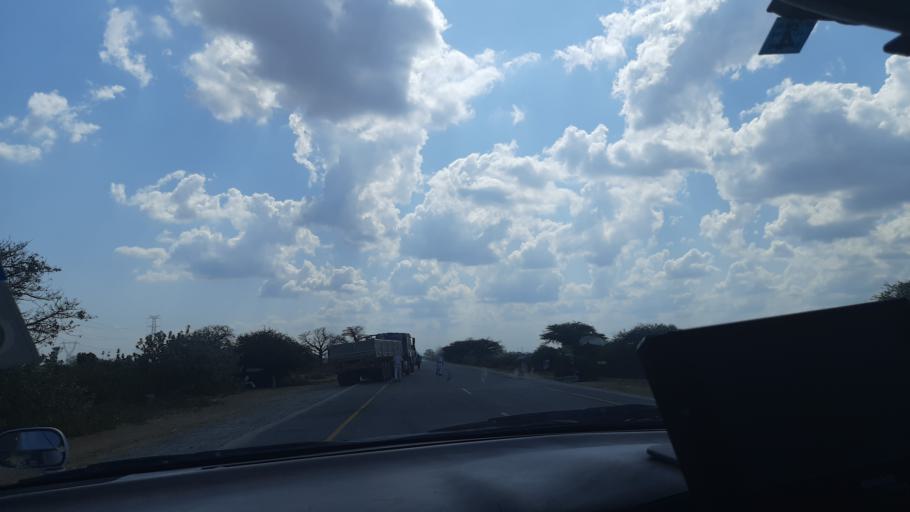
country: TZ
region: Singida
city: Kintinku
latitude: -5.9125
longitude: 35.2404
